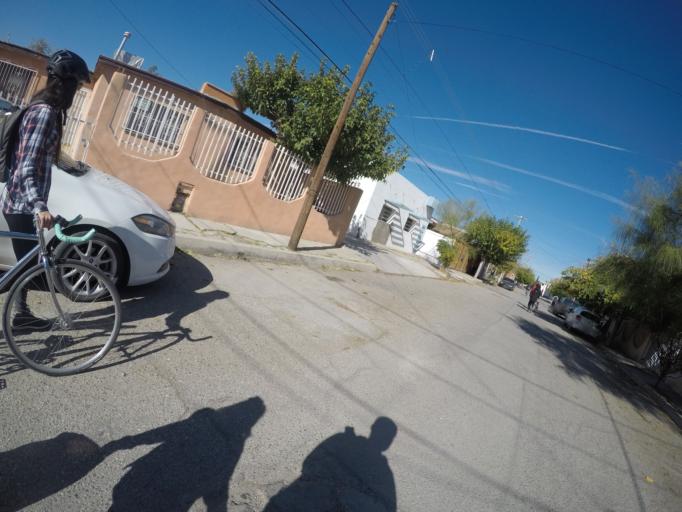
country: MX
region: Chihuahua
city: Ciudad Juarez
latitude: 31.7279
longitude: -106.4309
